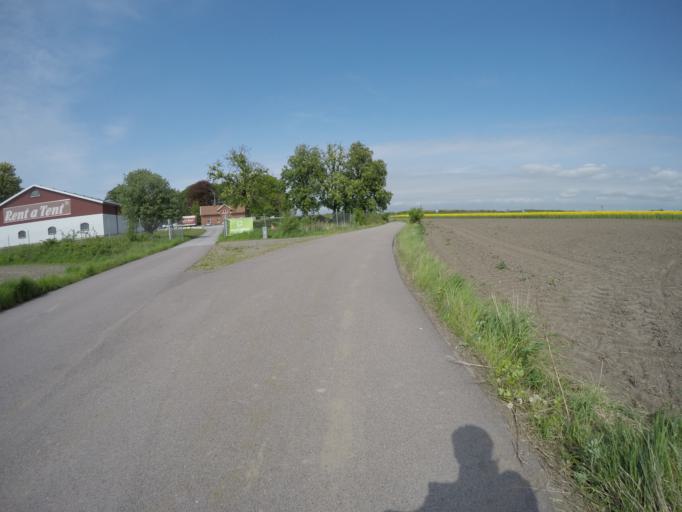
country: SE
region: Skane
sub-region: Malmo
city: Tygelsjo
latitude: 55.5452
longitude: 13.0137
